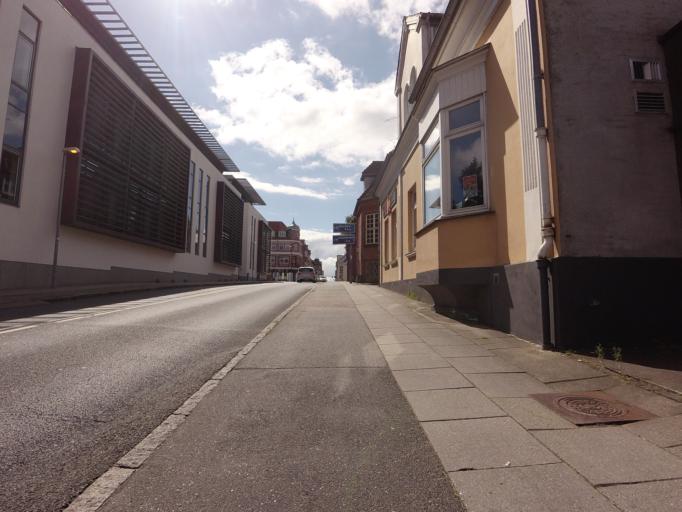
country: DK
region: Central Jutland
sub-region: Silkeborg Kommune
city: Silkeborg
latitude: 56.1687
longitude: 9.5437
